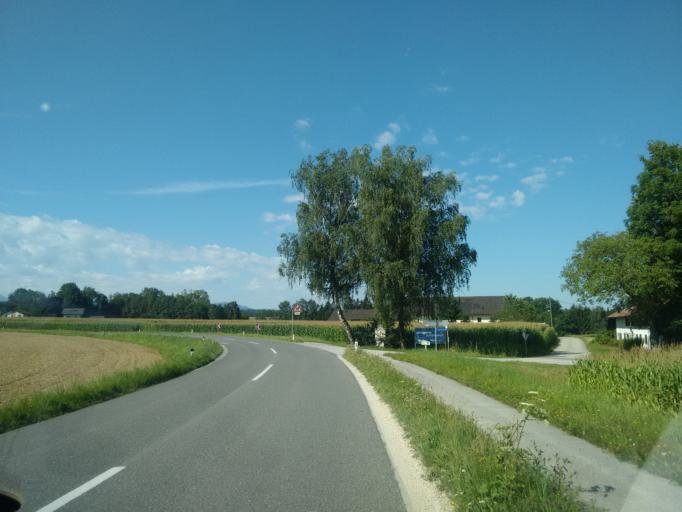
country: AT
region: Upper Austria
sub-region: Politischer Bezirk Steyr-Land
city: Pfarrkirchen bei Bad Hall
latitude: 48.0210
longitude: 14.1894
